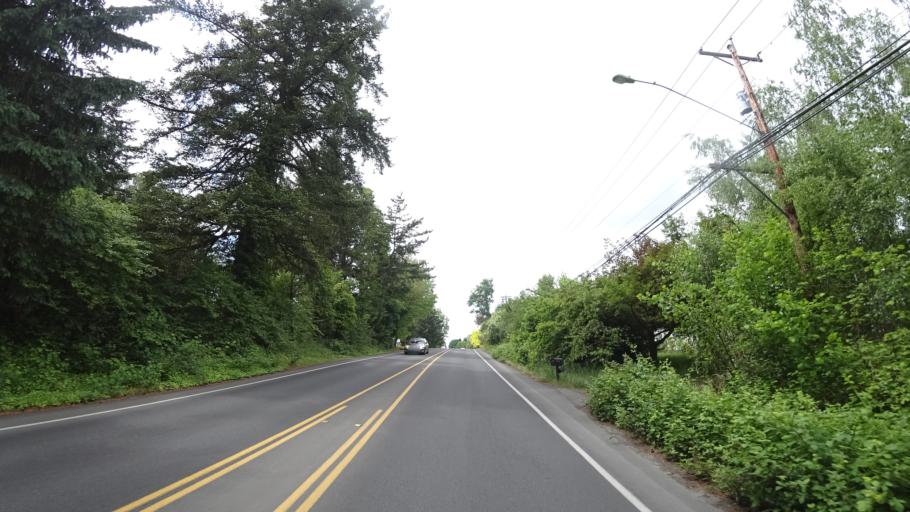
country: US
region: Oregon
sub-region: Washington County
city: Rockcreek
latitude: 45.5309
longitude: -122.8752
